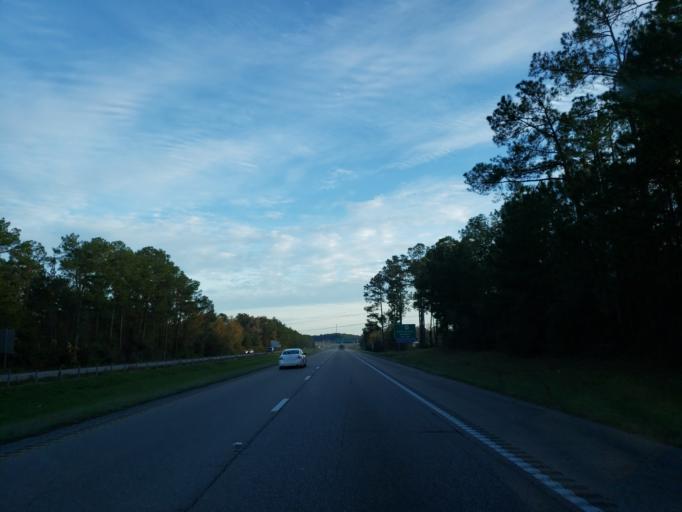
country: US
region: Mississippi
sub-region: Lamar County
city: West Hattiesburg
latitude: 31.2515
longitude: -89.3314
